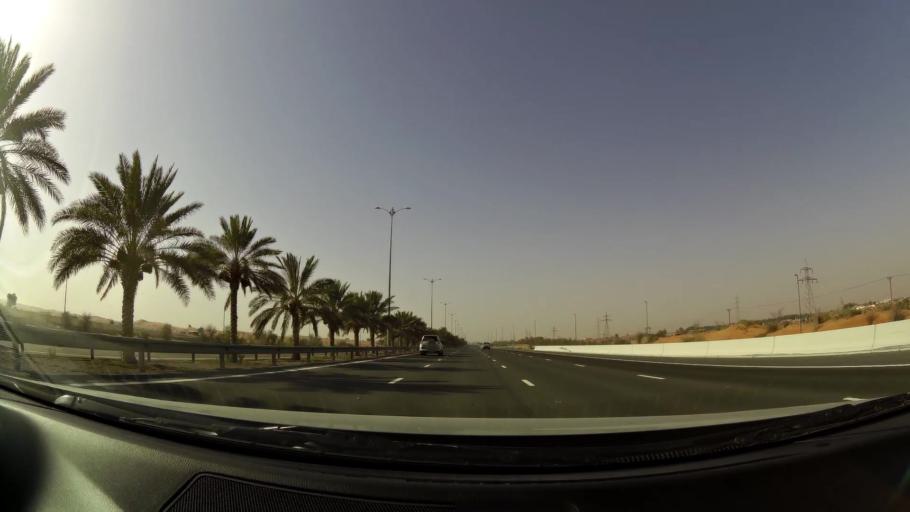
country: OM
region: Al Buraimi
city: Al Buraymi
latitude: 24.5193
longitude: 55.7627
